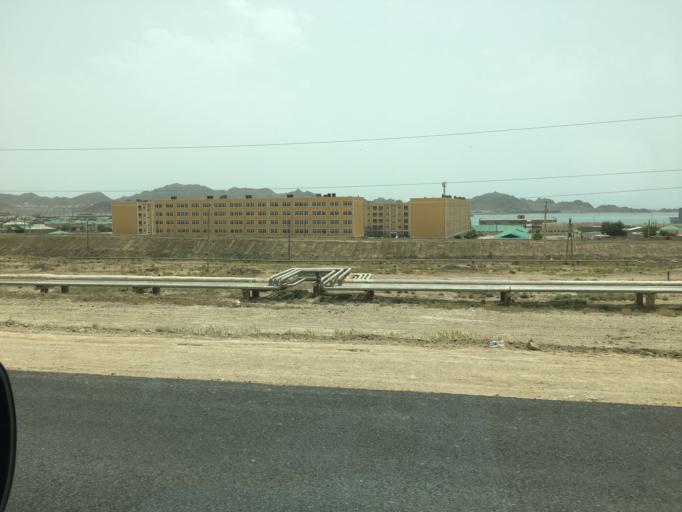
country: TM
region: Balkan
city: Turkmenbasy
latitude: 40.0128
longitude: 53.0613
